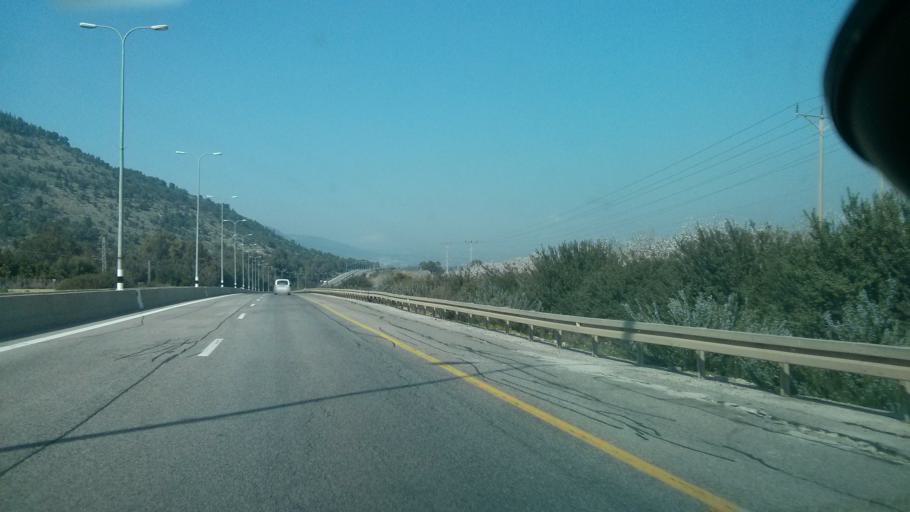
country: IL
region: Northern District
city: Rosh Pinna
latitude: 33.0771
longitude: 35.5758
